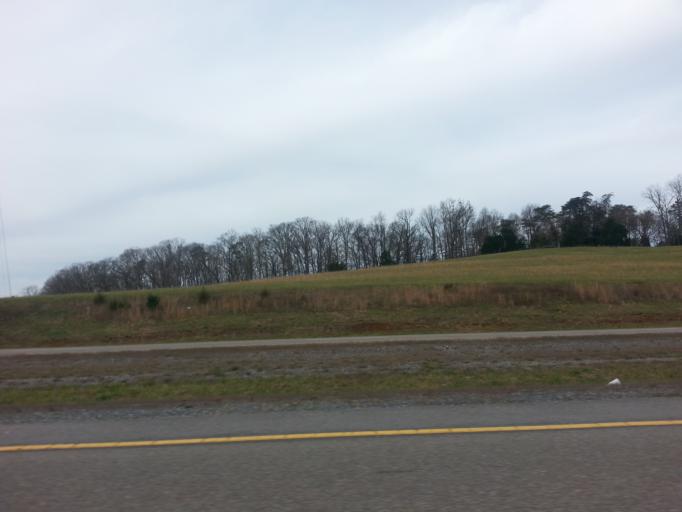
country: US
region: Tennessee
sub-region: Cocke County
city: Newport
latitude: 35.9962
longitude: -83.1075
